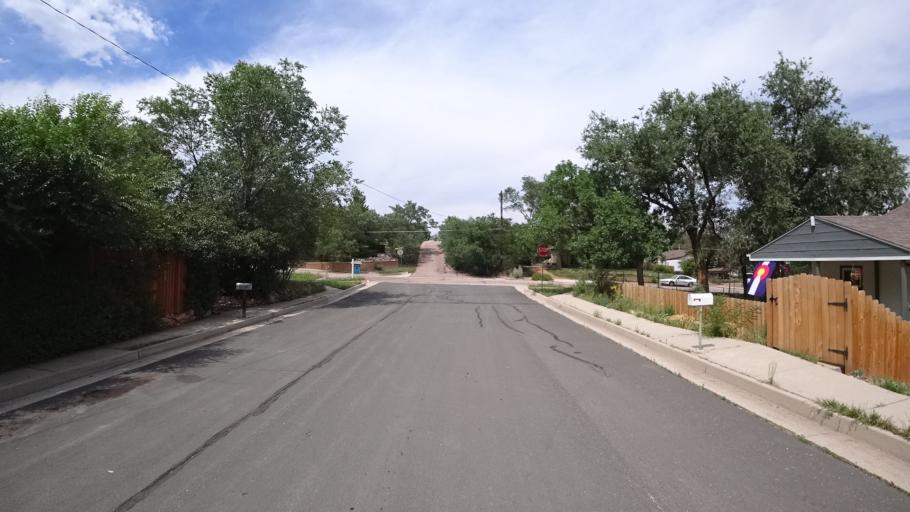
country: US
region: Colorado
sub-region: El Paso County
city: Colorado Springs
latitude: 38.8639
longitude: -104.8376
